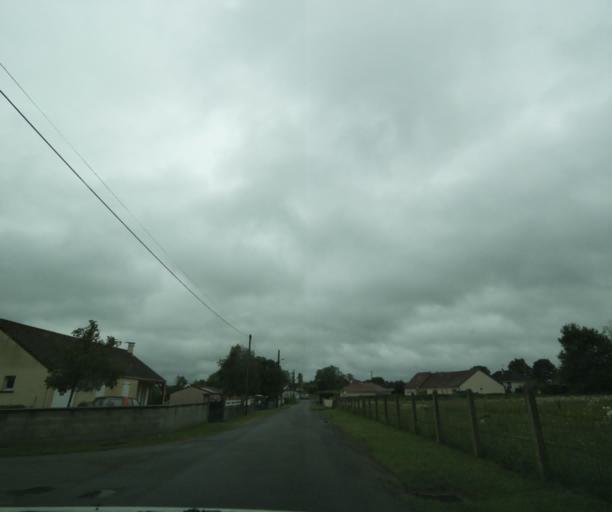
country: FR
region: Bourgogne
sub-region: Departement de Saone-et-Loire
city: Palinges
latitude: 46.5669
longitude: 4.2153
